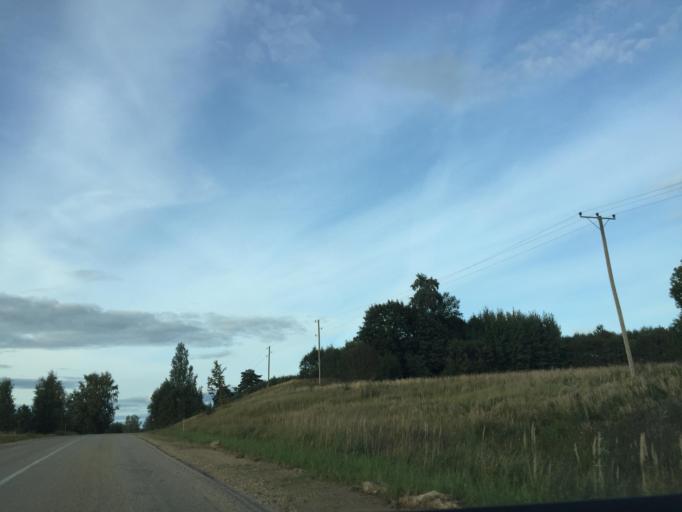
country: LV
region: Viesite
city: Viesite
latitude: 56.3122
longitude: 25.4486
